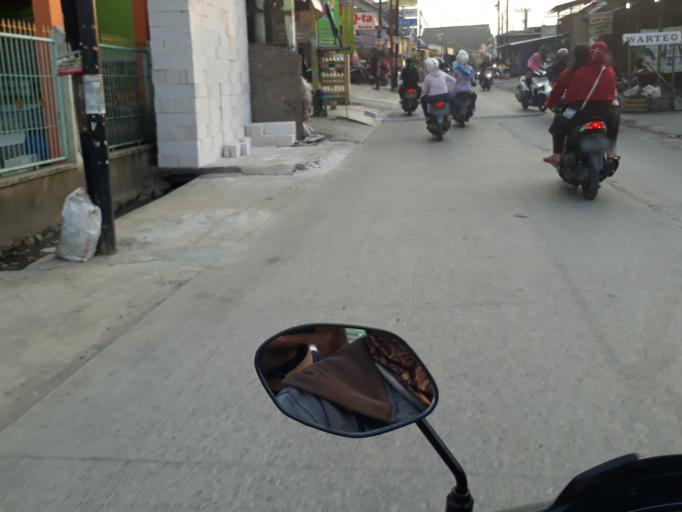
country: ID
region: West Java
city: Bekasi
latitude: -6.2435
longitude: 107.0469
